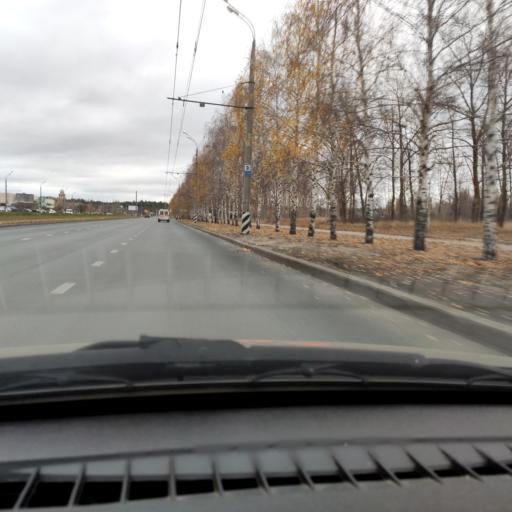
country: RU
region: Samara
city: Tol'yatti
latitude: 53.4987
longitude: 49.2813
